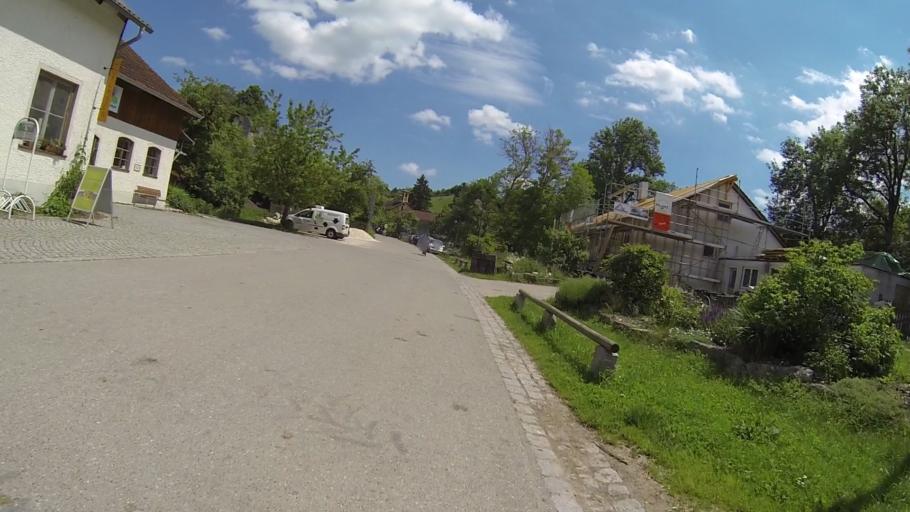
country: DE
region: Baden-Wuerttemberg
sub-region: Regierungsbezirk Stuttgart
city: Herbrechtingen
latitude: 48.6008
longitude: 10.1790
